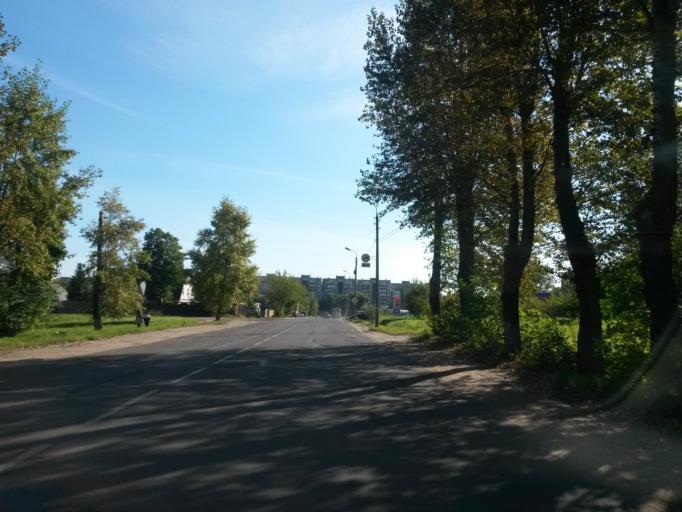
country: RU
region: Jaroslavl
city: Yaroslavl
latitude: 57.5779
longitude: 39.8684
